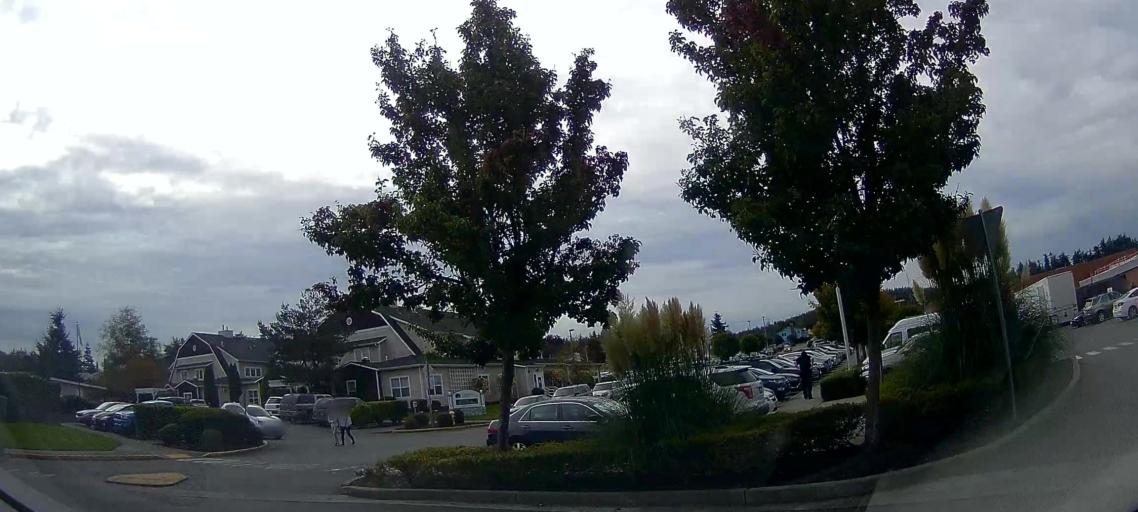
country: US
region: Washington
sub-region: Skagit County
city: Anacortes
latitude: 48.5014
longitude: -122.6145
